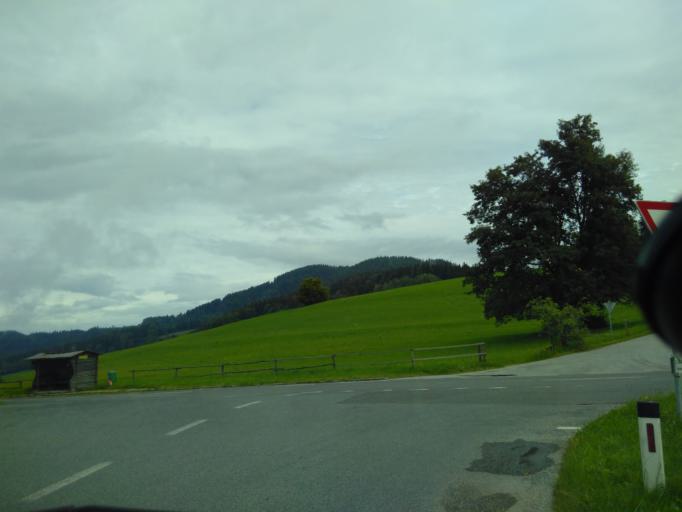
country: AT
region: Styria
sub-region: Politischer Bezirk Graz-Umgebung
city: Semriach
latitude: 47.2686
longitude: 15.4152
